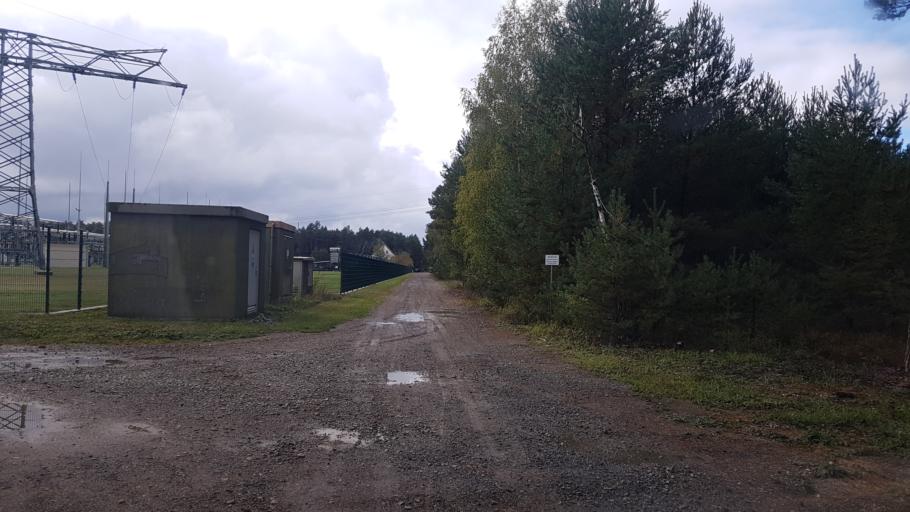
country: DE
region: Brandenburg
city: Grossraschen
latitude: 51.6086
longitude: 14.0264
